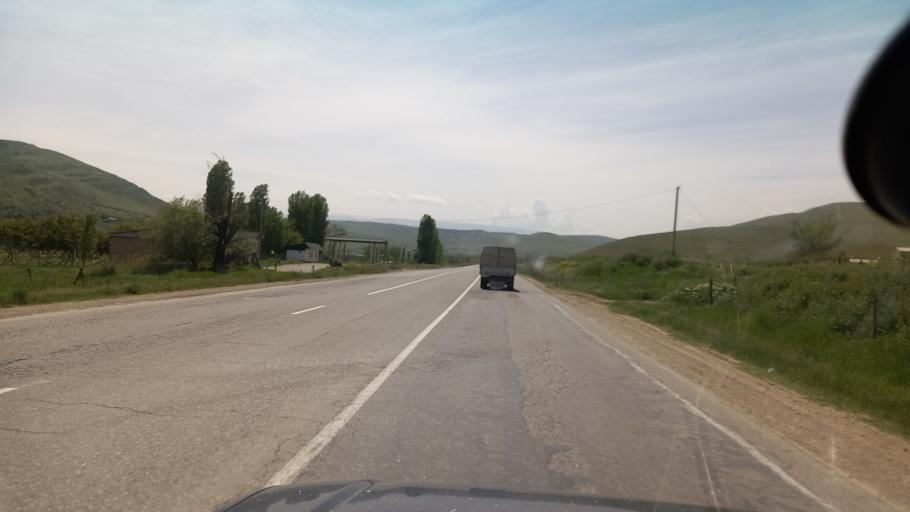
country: RU
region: Dagestan
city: Manas
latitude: 42.7062
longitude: 47.6319
